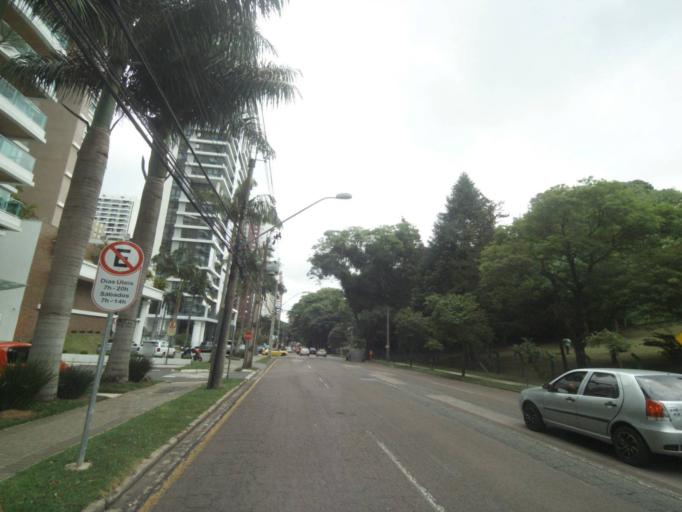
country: BR
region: Parana
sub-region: Curitiba
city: Curitiba
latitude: -25.4327
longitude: -49.3020
